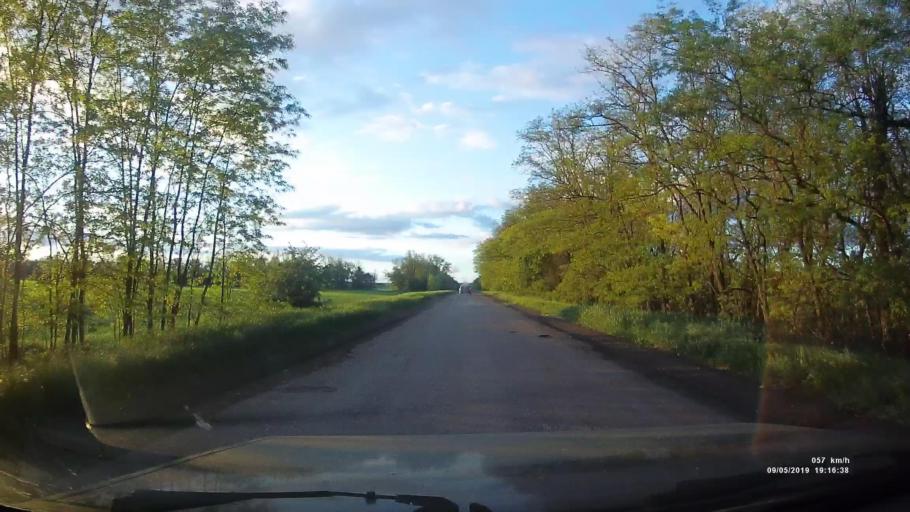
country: RU
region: Krasnodarskiy
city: Kanelovskaya
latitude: 46.7793
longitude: 39.2116
